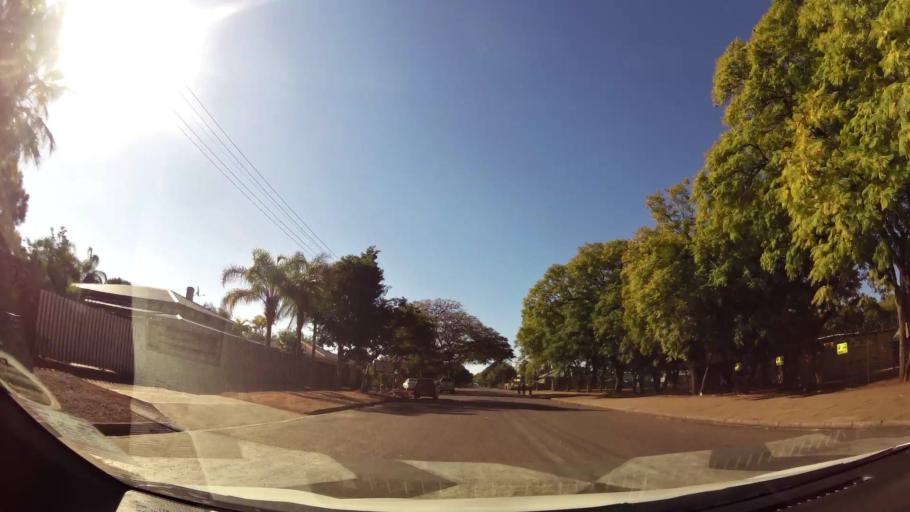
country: ZA
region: Limpopo
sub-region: Waterberg District Municipality
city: Mokopane
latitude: -24.1844
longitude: 29.0036
